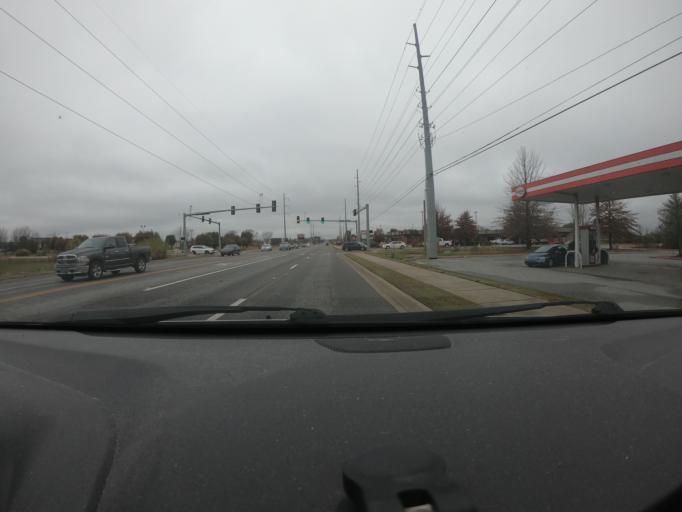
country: US
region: Arkansas
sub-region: Benton County
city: Bentonville
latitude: 36.3576
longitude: -94.2387
